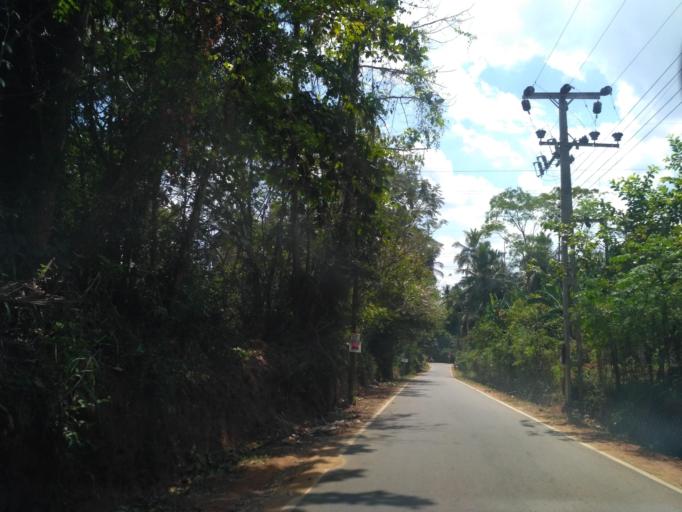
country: LK
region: North Western
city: Kuliyapitiya
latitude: 7.3280
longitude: 80.0626
